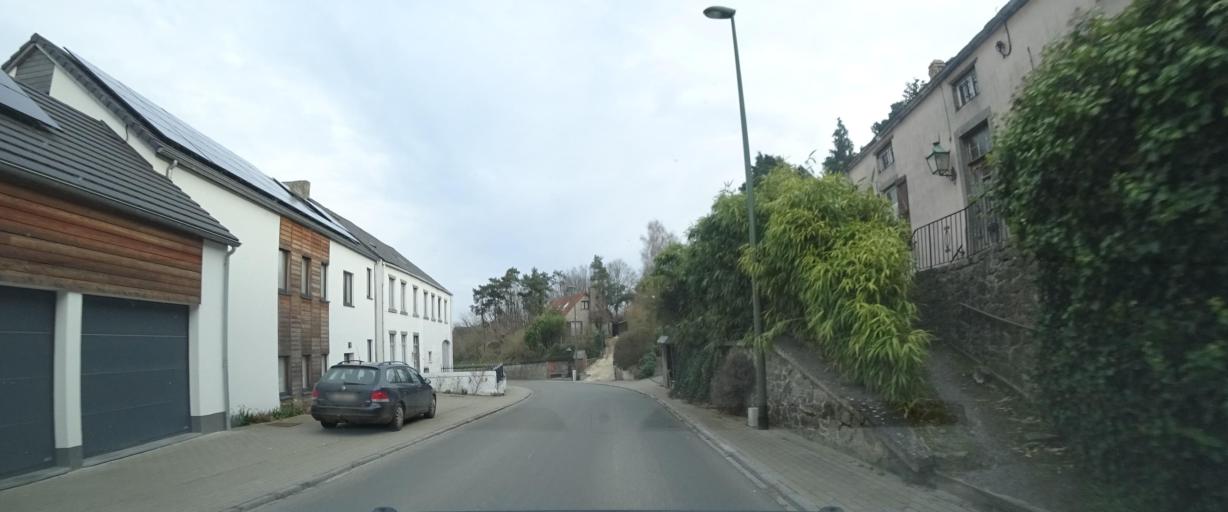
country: BE
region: Wallonia
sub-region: Province du Brabant Wallon
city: Chastre
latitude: 50.6026
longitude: 4.6095
